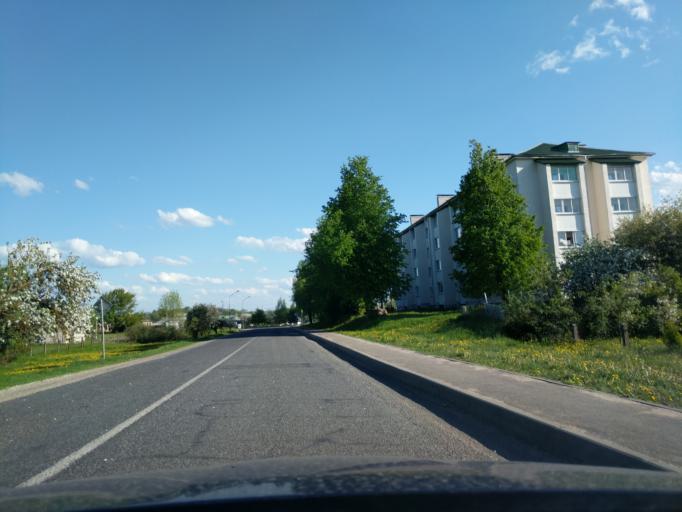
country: BY
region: Minsk
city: Myadzyel
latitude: 54.8895
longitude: 26.9140
